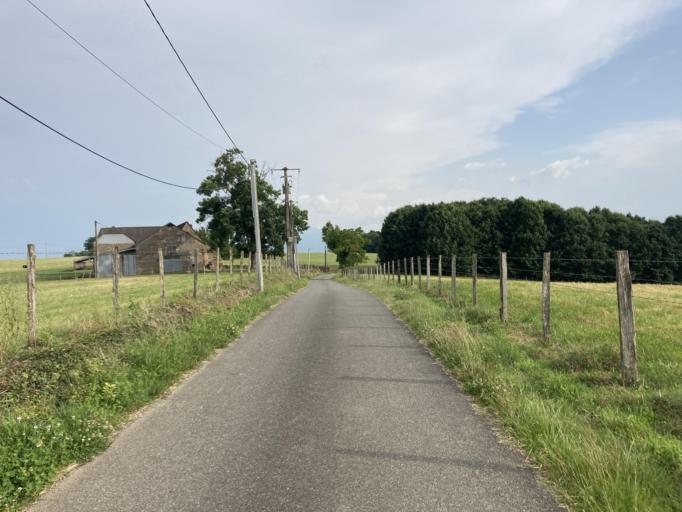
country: FR
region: Aquitaine
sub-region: Departement des Pyrenees-Atlantiques
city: Ledeuix
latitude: 43.2509
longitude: -0.6213
